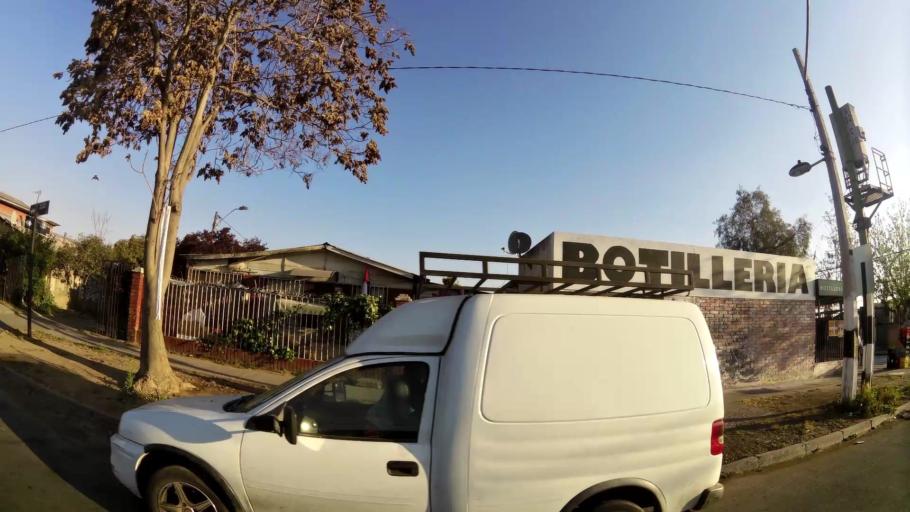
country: CL
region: Santiago Metropolitan
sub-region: Provincia de Santiago
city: La Pintana
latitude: -33.5468
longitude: -70.6249
